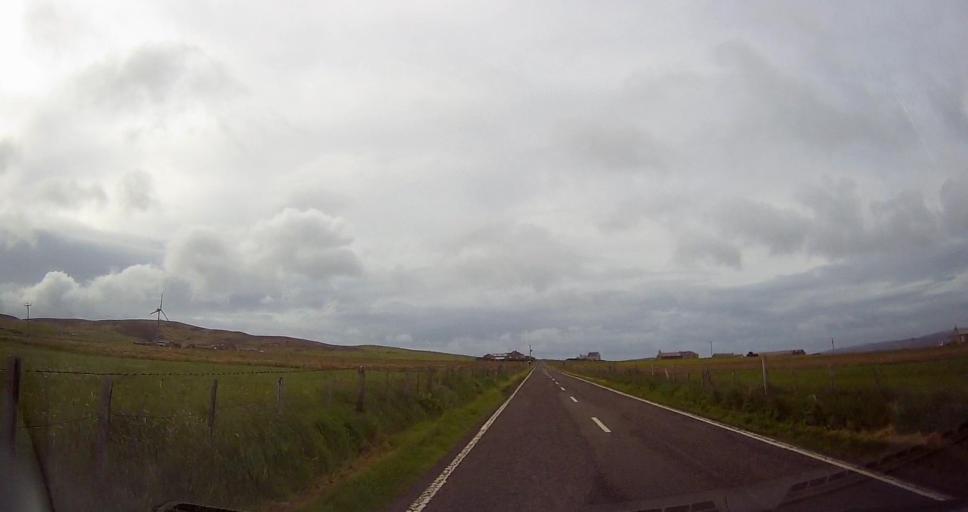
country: GB
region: Scotland
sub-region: Orkney Islands
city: Stromness
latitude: 58.9355
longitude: -3.2102
